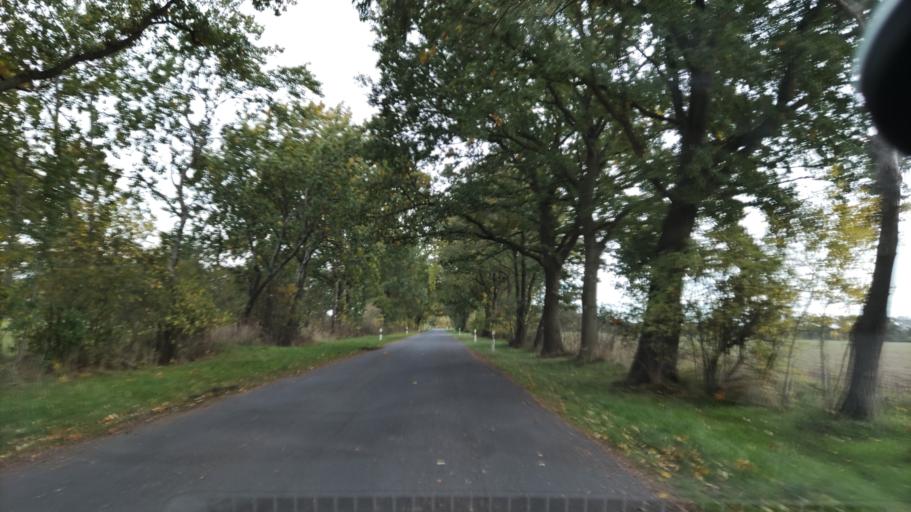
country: DE
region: Lower Saxony
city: Neu Darchau
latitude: 53.3491
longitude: 10.8638
